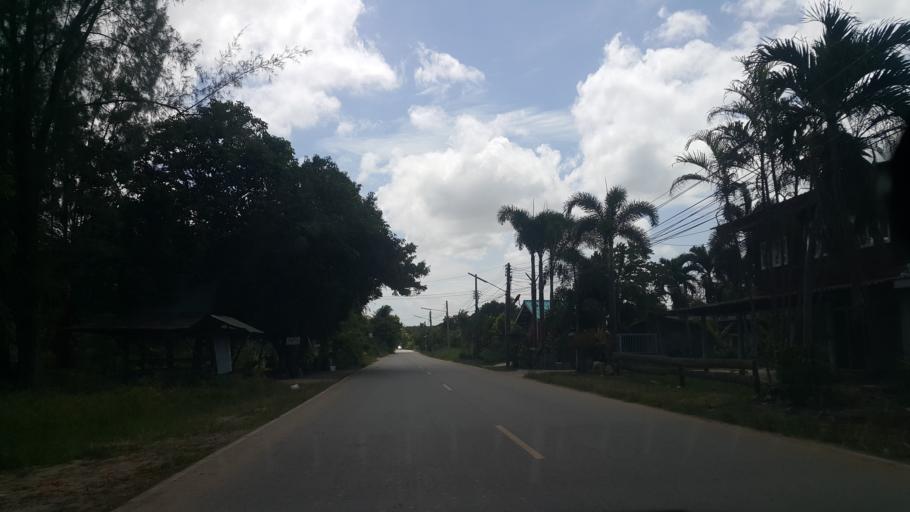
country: TH
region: Rayong
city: Ban Chang
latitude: 12.7974
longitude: 101.0266
